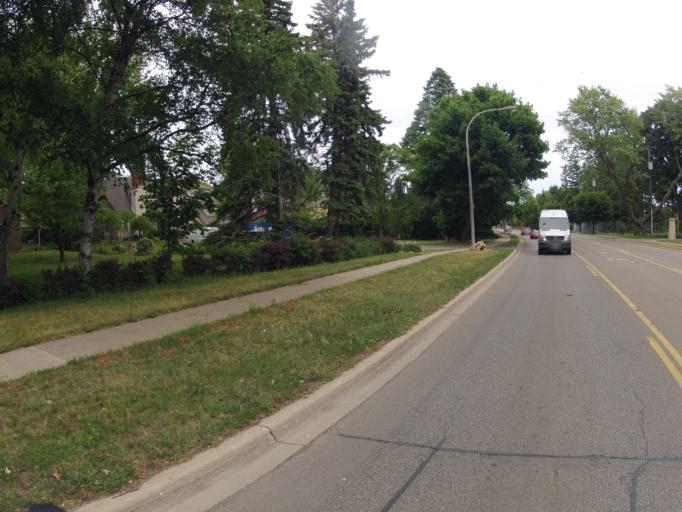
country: CA
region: Ontario
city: Burlington
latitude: 43.3358
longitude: -79.7727
